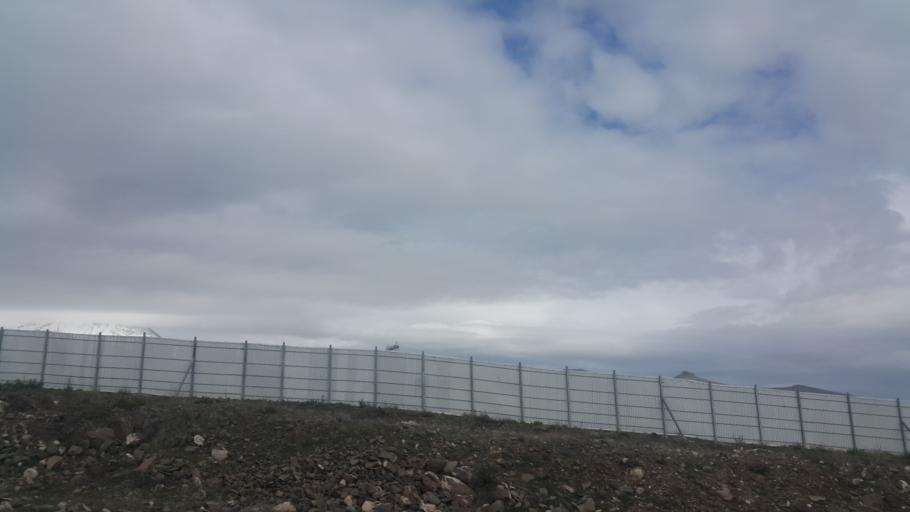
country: TR
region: Aksaray
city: Taspinar
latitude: 38.0799
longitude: 34.0328
